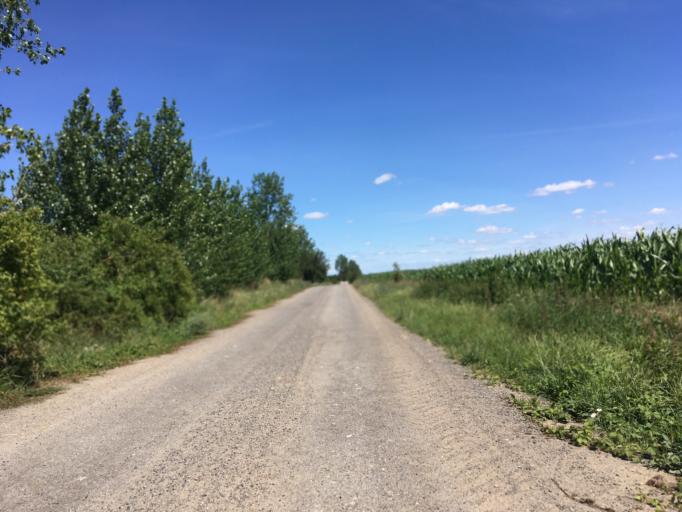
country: DE
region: Brandenburg
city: Grunow
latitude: 53.3266
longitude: 13.9641
